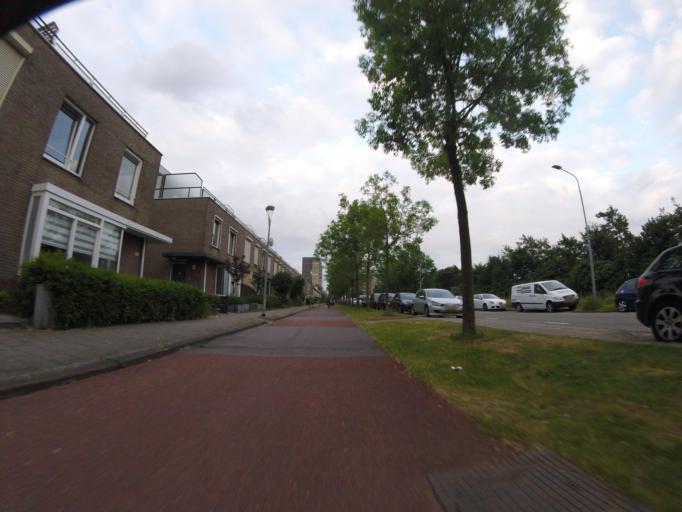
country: NL
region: North Holland
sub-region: Gemeente Haarlemmermeer
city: Hoofddorp
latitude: 52.2927
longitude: 4.6676
